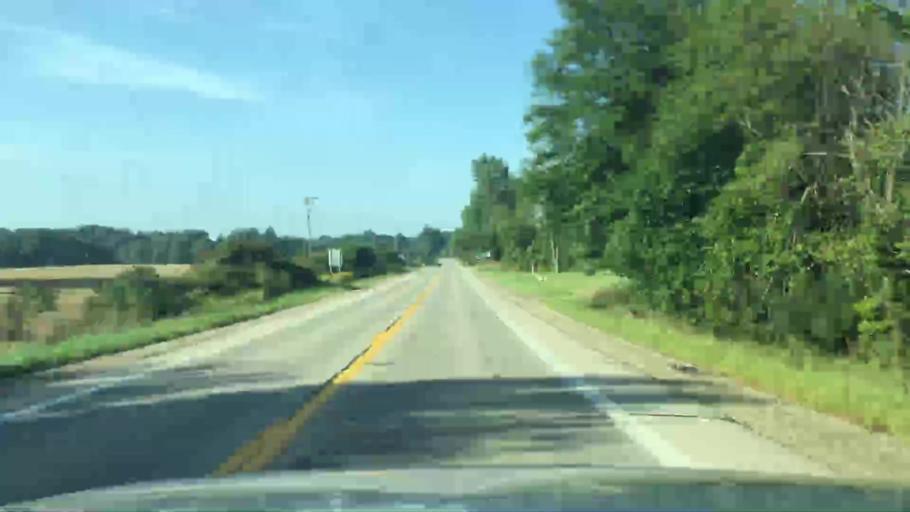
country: US
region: Michigan
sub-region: Lenawee County
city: Manitou Beach-Devils Lake
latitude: 41.9692
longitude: -84.3608
